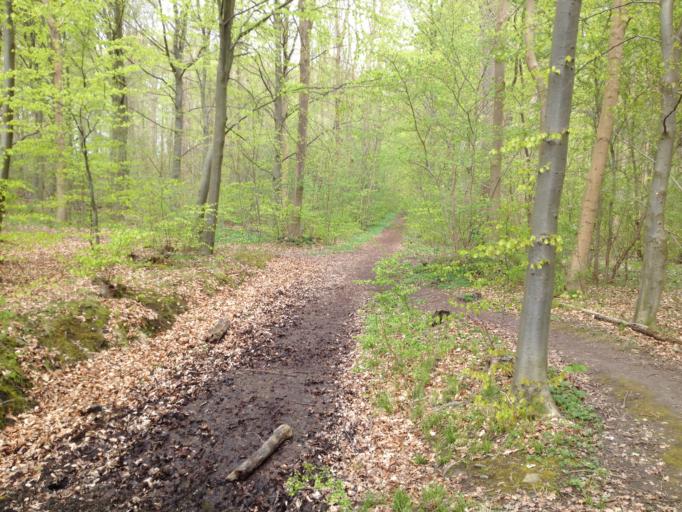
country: DK
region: Capital Region
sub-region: Fredensborg Kommune
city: Niva
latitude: 55.9427
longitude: 12.5123
